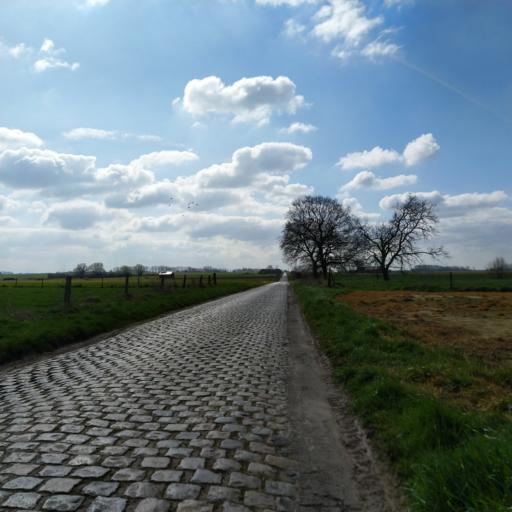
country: BE
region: Wallonia
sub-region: Province du Hainaut
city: Jurbise
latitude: 50.5608
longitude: 3.9489
